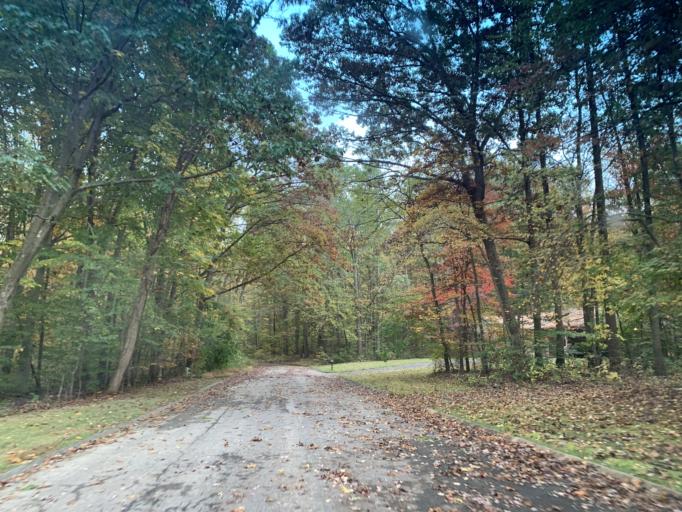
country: US
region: Maryland
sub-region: Harford County
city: South Bel Air
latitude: 39.5718
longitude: -76.3266
